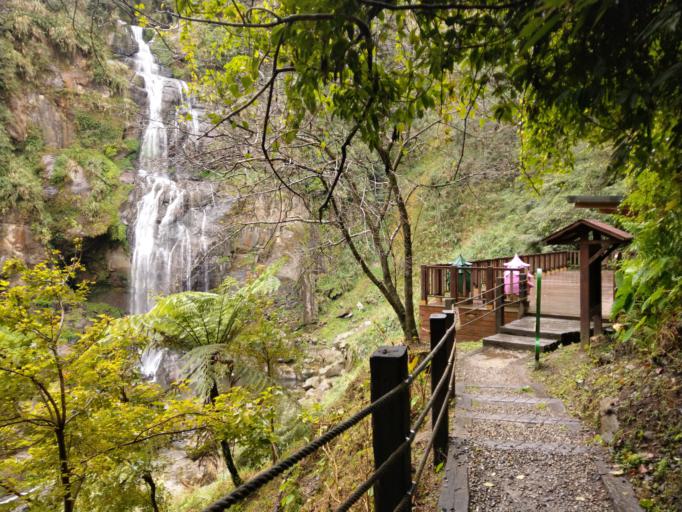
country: TW
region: Taiwan
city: Lugu
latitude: 23.6380
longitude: 120.7836
